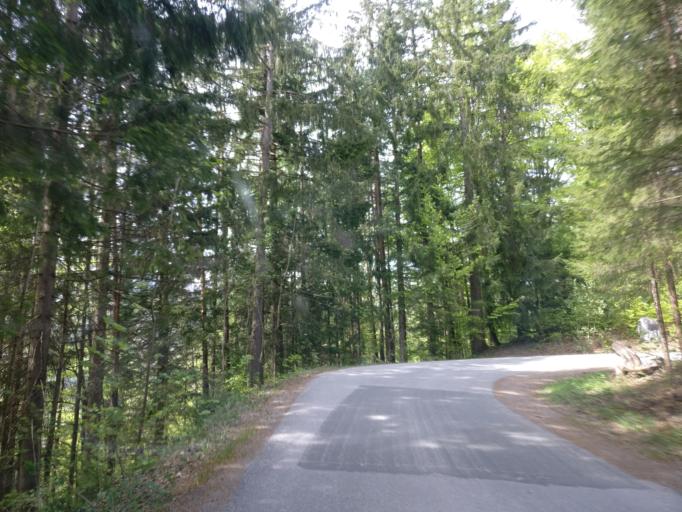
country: AT
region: Salzburg
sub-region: Politischer Bezirk Sankt Johann im Pongau
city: Werfen
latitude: 47.4743
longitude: 13.1988
